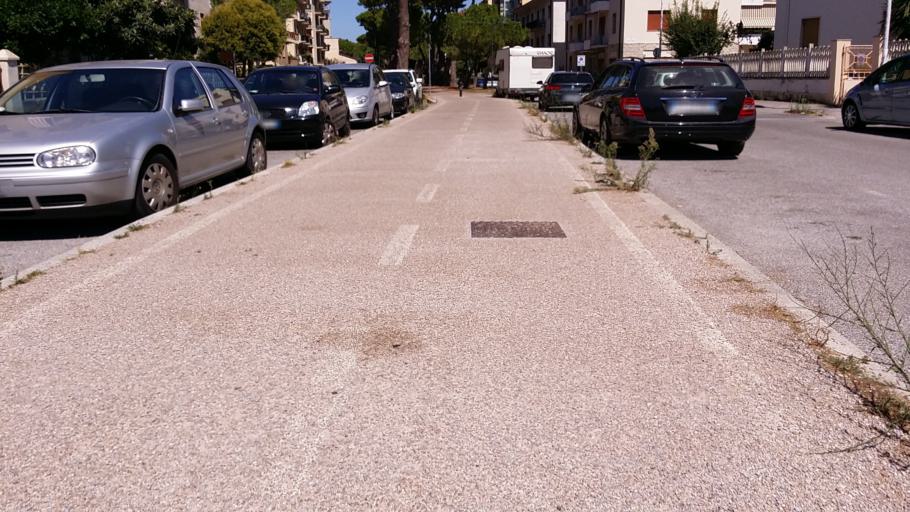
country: IT
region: Tuscany
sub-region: Provincia di Livorno
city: Livorno
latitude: 43.5337
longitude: 10.3195
